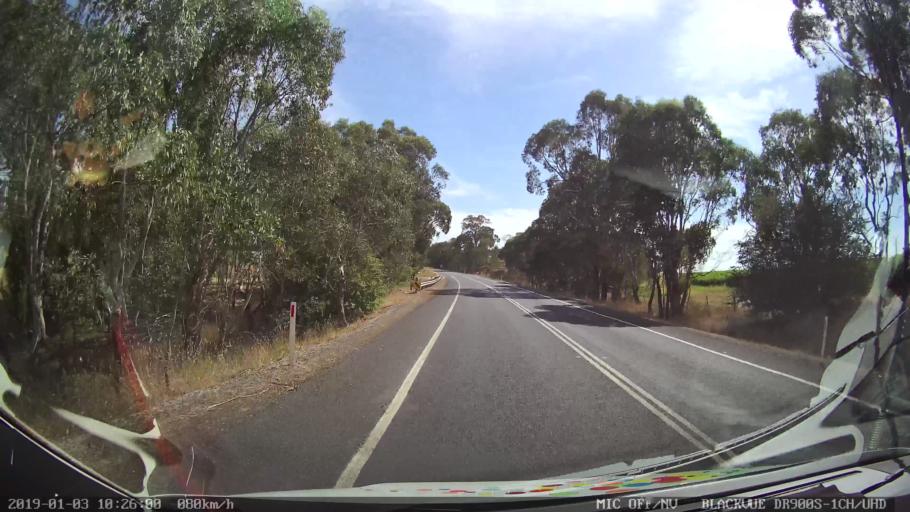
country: AU
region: New South Wales
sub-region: Young
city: Young
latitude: -34.4176
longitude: 148.2463
